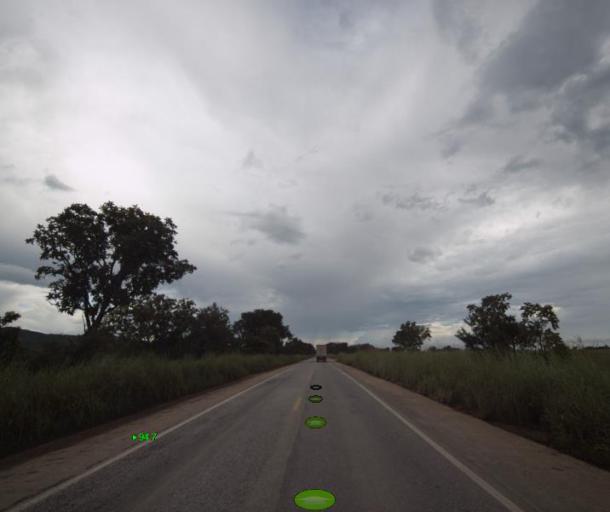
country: BR
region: Goias
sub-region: Porangatu
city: Porangatu
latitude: -13.6053
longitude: -49.0421
